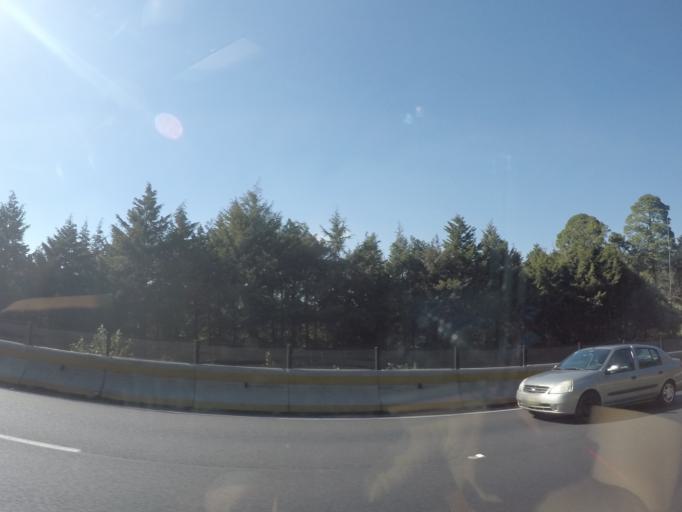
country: MX
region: Mexico City
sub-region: Cuajimalpa de Morelos
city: San Lorenzo Acopilco
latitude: 19.3275
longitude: -99.3168
